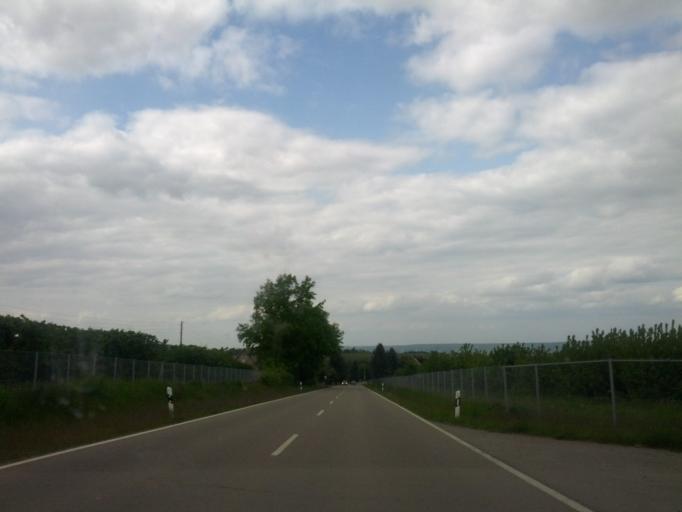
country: DE
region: Saxony
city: Kreischa
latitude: 50.9550
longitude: 13.7949
